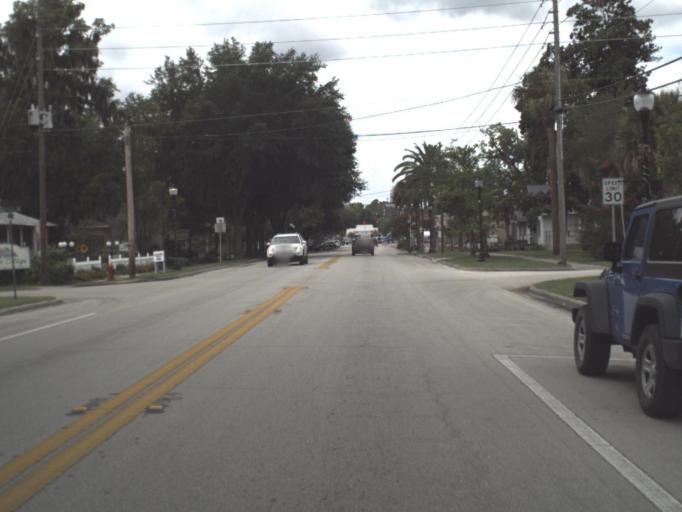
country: US
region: Florida
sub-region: Alachua County
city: High Springs
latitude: 29.8290
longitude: -82.5957
